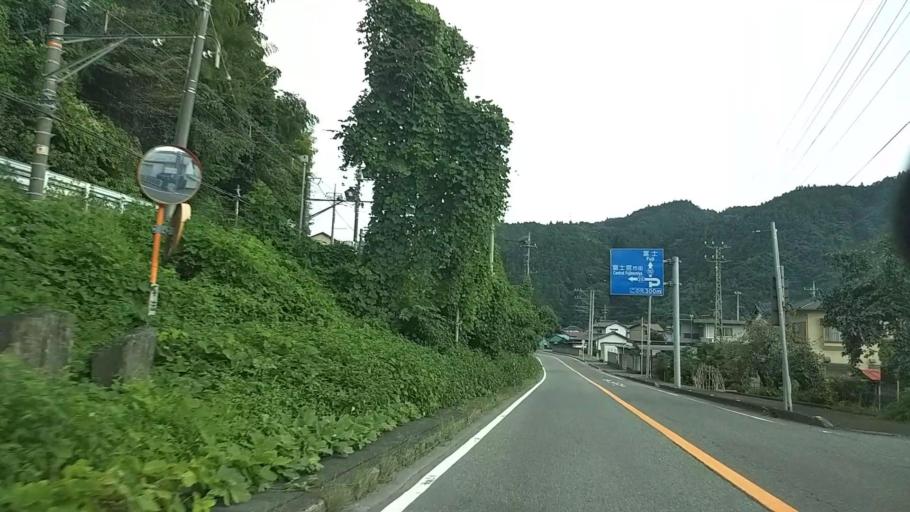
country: JP
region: Shizuoka
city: Fujinomiya
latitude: 35.1958
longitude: 138.5647
